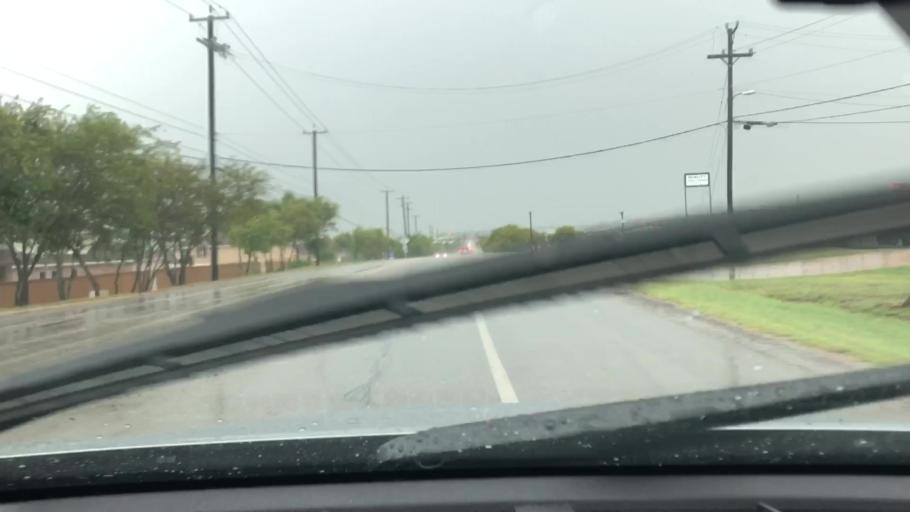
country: US
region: Texas
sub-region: Bexar County
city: Converse
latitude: 29.4722
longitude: -98.3131
